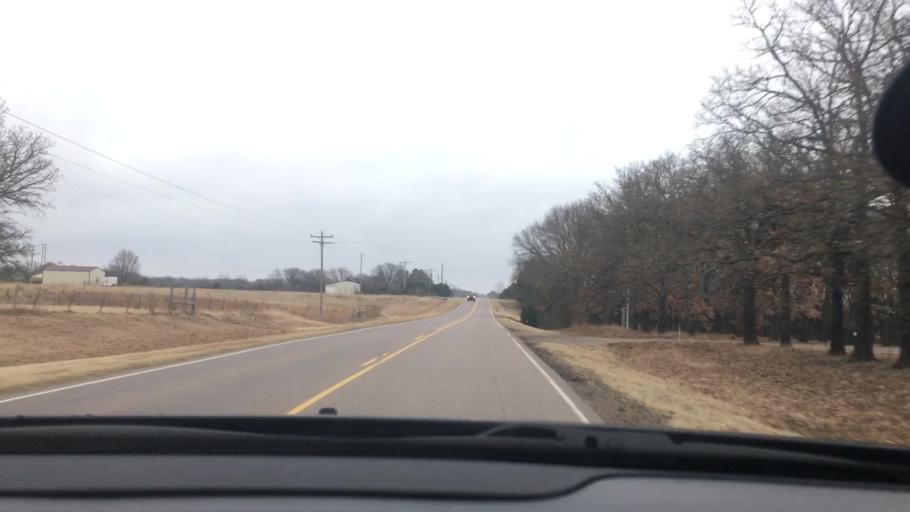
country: US
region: Oklahoma
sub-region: Johnston County
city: Tishomingo
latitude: 34.2735
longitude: -96.6711
